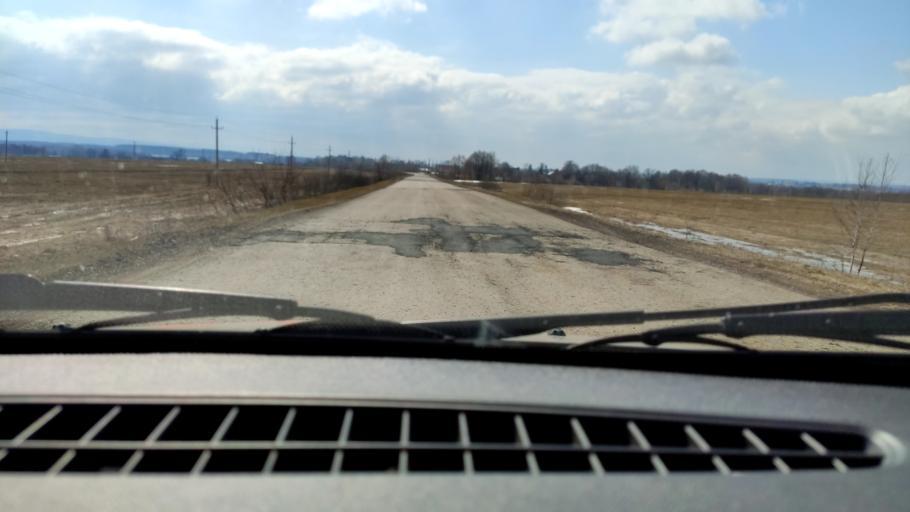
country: RU
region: Bashkortostan
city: Kudeyevskiy
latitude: 54.8386
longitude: 56.7942
